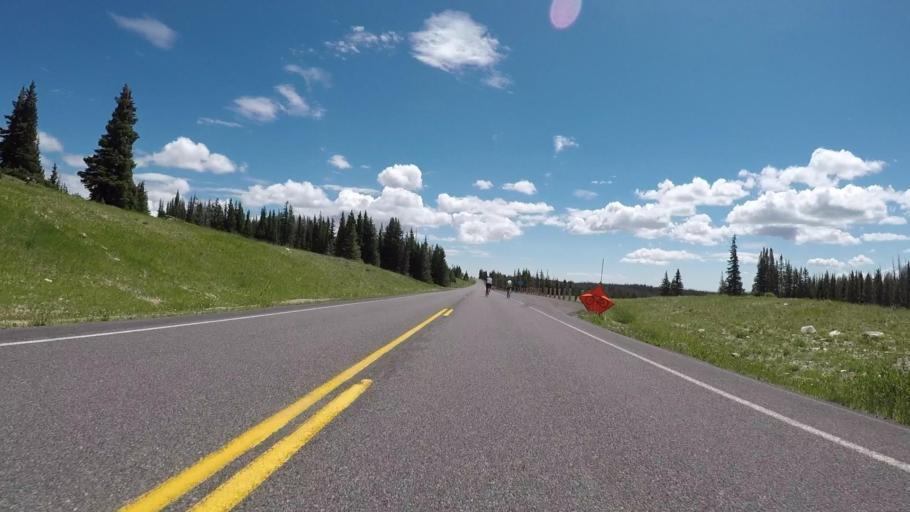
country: US
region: Wyoming
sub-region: Carbon County
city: Saratoga
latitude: 41.3511
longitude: -106.2824
